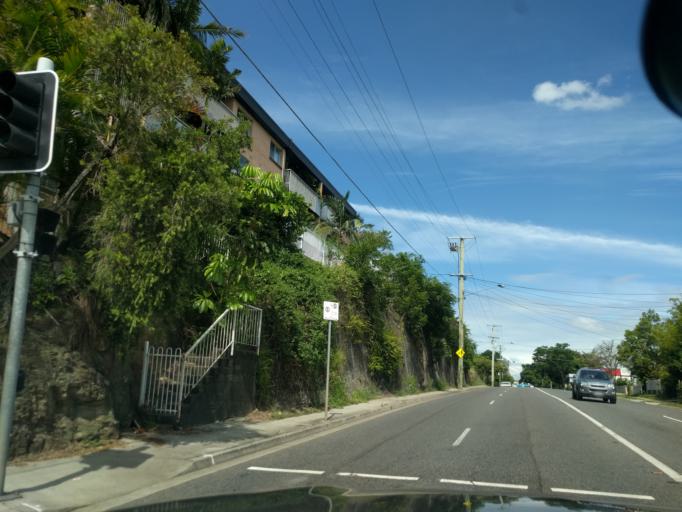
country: AU
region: Queensland
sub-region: Brisbane
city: Windsor
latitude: -27.4376
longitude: 153.0272
